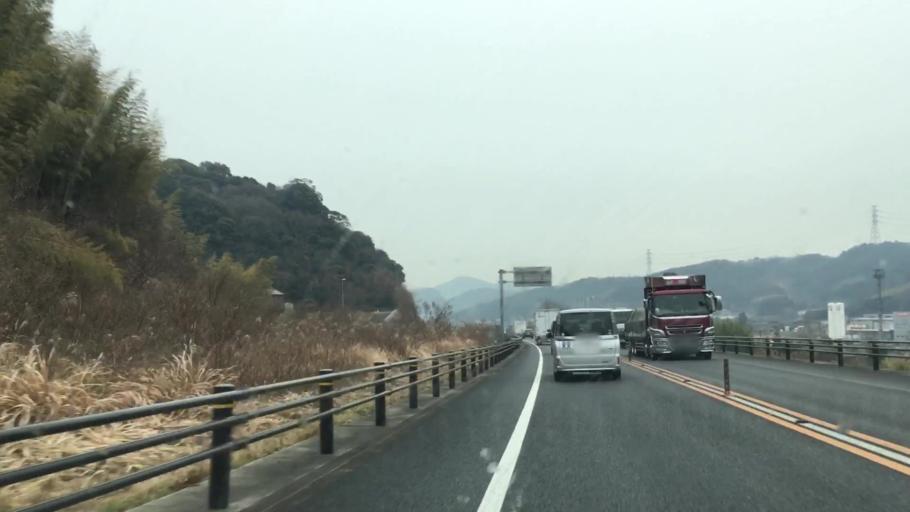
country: JP
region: Aichi
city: Gamagori
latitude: 34.8470
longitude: 137.1470
